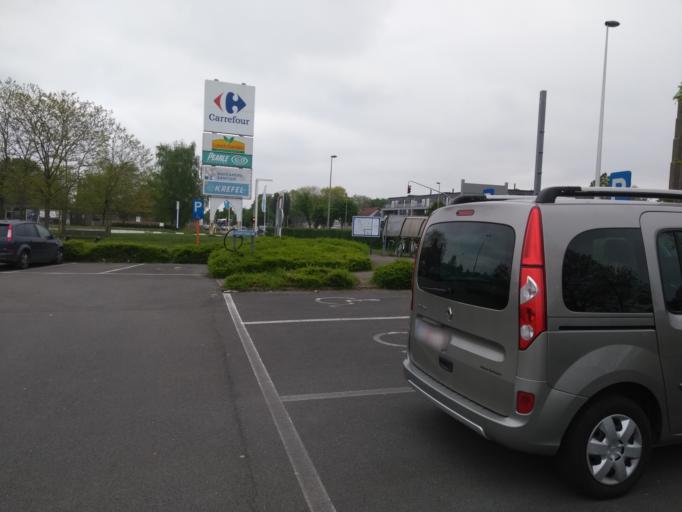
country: BE
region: Flanders
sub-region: Provincie Oost-Vlaanderen
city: Destelbergen
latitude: 51.0744
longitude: 3.7779
